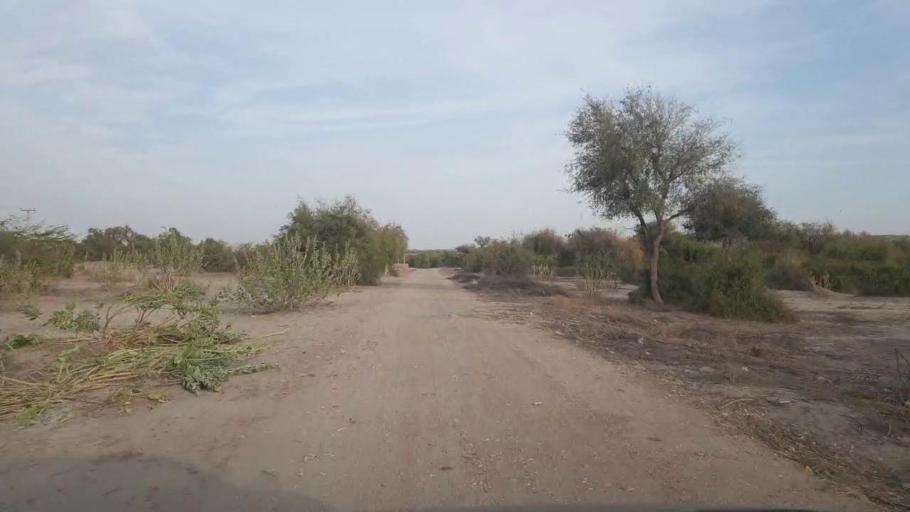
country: PK
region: Sindh
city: Nabisar
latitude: 25.0994
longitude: 69.6703
